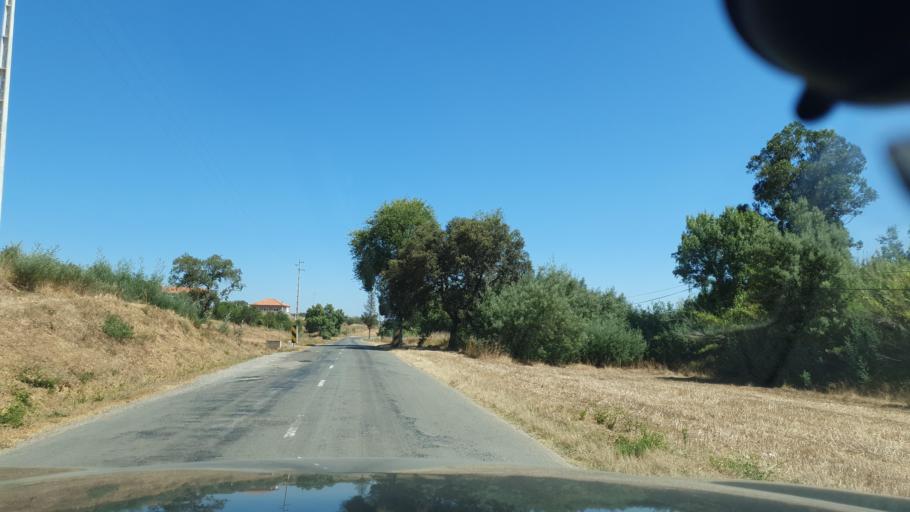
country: PT
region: Faro
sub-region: Monchique
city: Monchique
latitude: 37.4546
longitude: -8.4868
